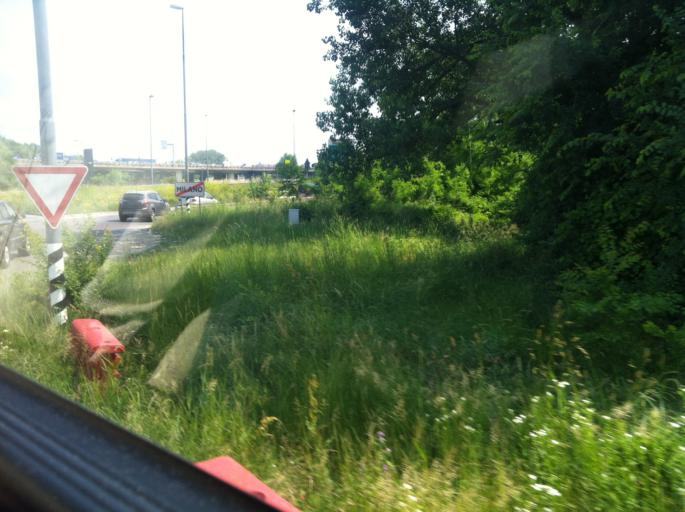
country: IT
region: Lombardy
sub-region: Citta metropolitana di Milano
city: Novegro-Tregarezzo-San Felice
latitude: 45.4768
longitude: 9.2497
